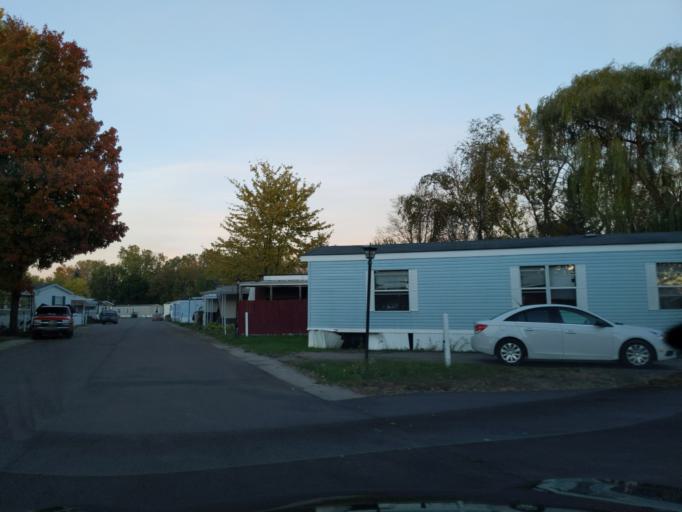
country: US
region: Michigan
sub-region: Ingham County
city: Edgemont Park
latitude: 42.7230
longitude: -84.5987
